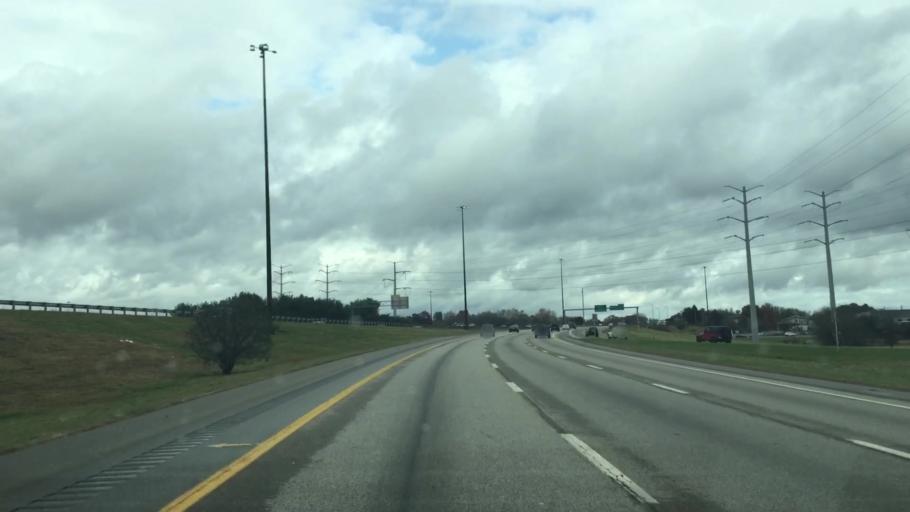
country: US
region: New Hampshire
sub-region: Rockingham County
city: Portsmouth
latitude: 43.0713
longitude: -70.7860
